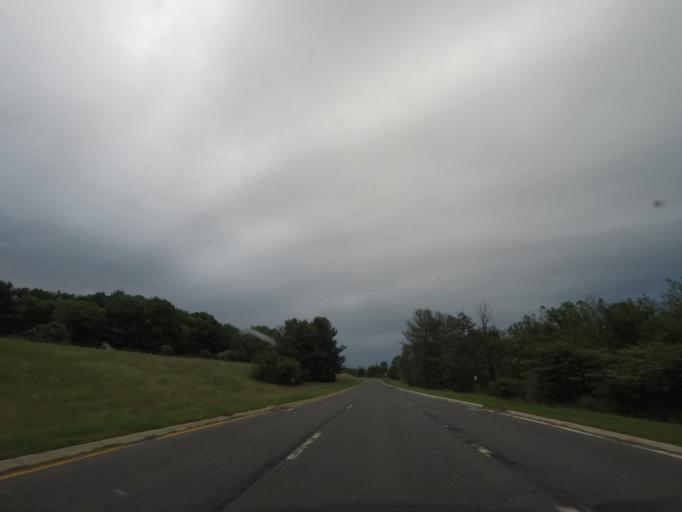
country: US
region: New York
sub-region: Columbia County
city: Chatham
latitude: 42.3566
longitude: -73.5760
